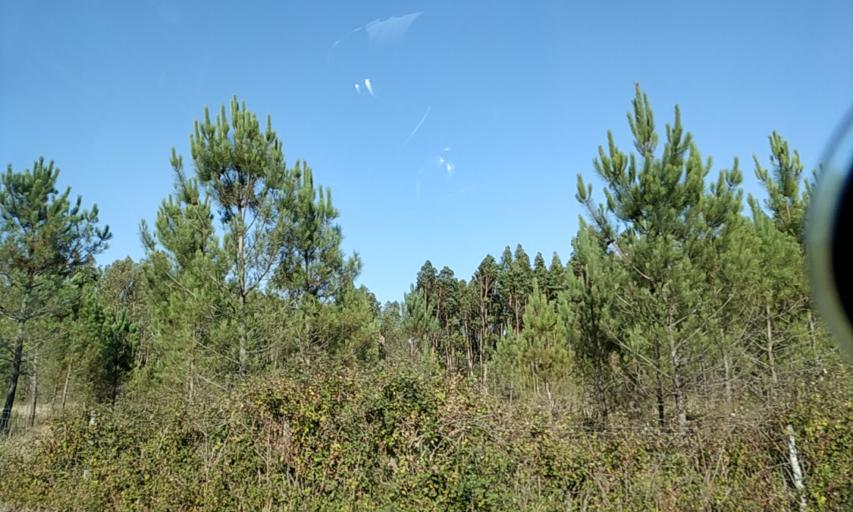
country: PT
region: Santarem
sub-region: Coruche
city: Coruche
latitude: 39.0211
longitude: -8.5616
